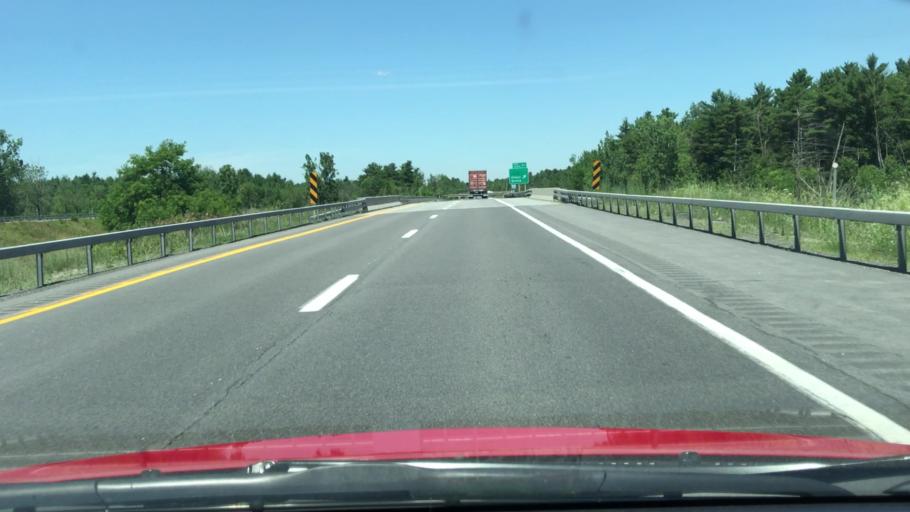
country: US
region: New York
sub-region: Clinton County
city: Champlain
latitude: 44.8840
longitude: -73.4514
